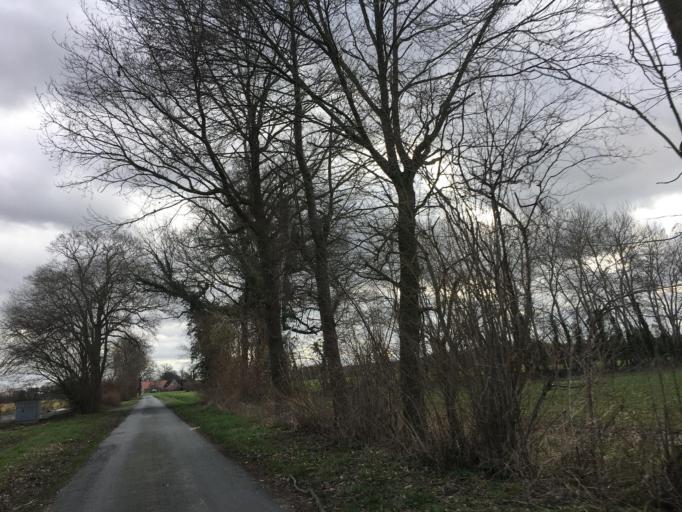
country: DE
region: North Rhine-Westphalia
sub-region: Regierungsbezirk Munster
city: Horstmar
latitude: 52.1138
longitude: 7.3099
